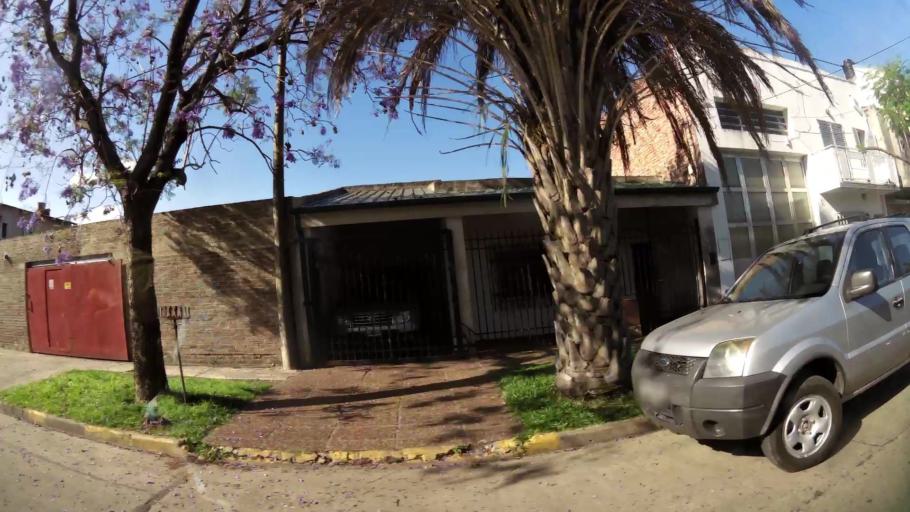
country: AR
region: Santa Fe
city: Santa Fe de la Vera Cruz
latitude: -31.6082
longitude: -60.6909
